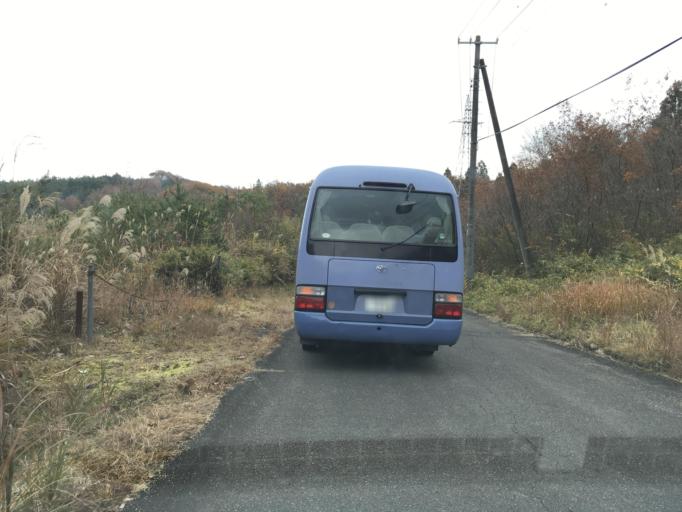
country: JP
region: Iwate
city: Ichinoseki
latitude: 38.7950
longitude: 140.9736
